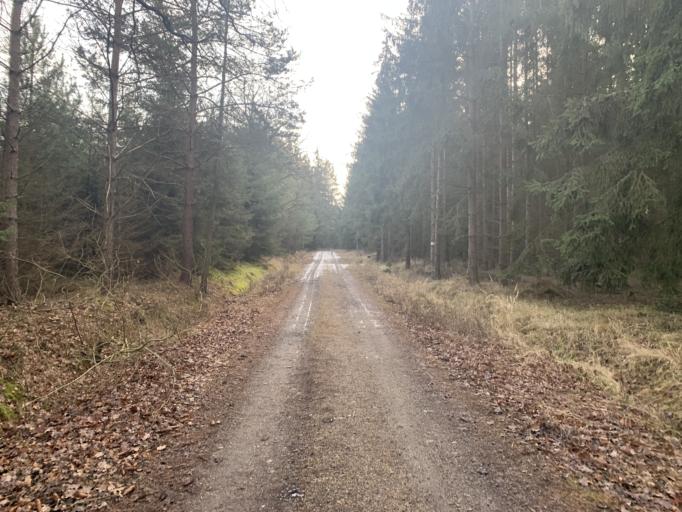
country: CZ
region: Plzensky
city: Zbiroh
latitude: 49.8279
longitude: 13.7975
